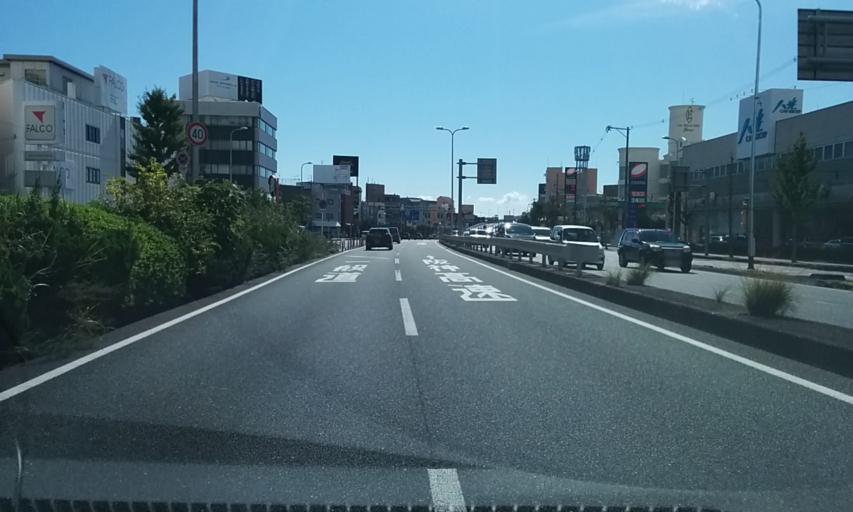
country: JP
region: Osaka
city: Ikeda
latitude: 34.7985
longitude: 135.4406
